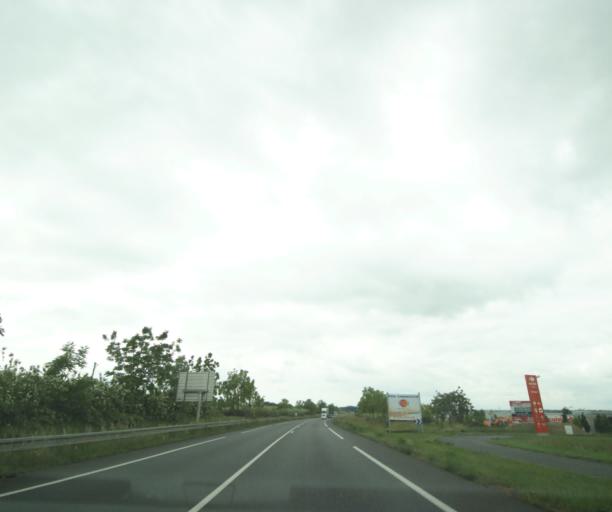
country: FR
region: Pays de la Loire
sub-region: Departement de Maine-et-Loire
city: Distre
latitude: 47.2336
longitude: -0.1123
